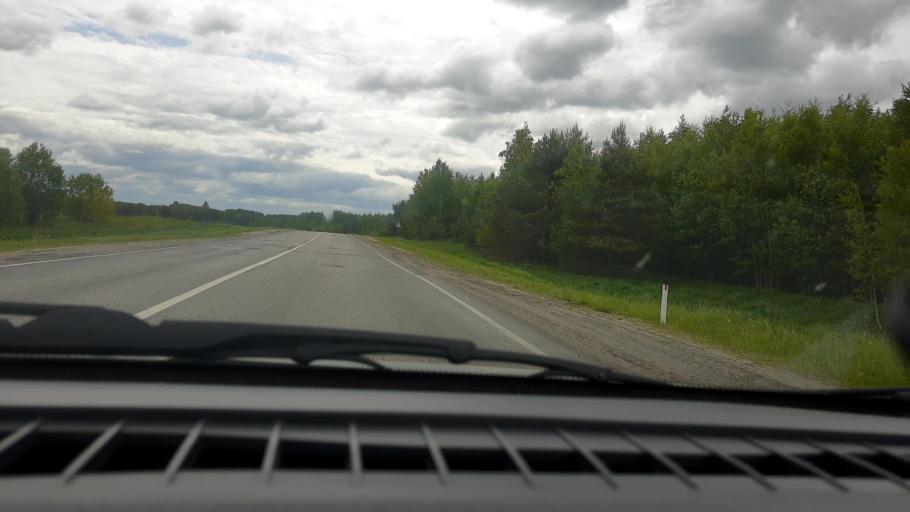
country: RU
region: Nizjnij Novgorod
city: Vladimirskoye
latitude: 56.9654
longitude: 45.1090
